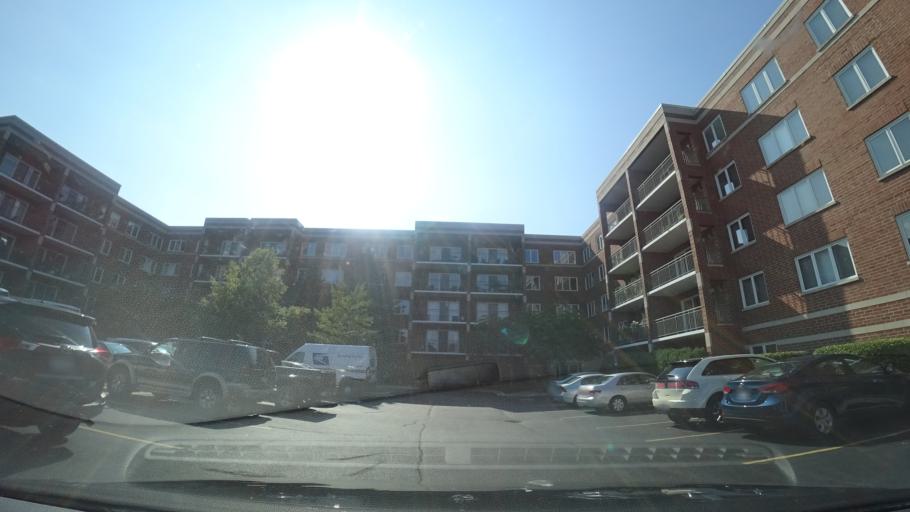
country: US
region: Illinois
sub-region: Cook County
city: Lincolnwood
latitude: 41.9788
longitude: -87.7372
